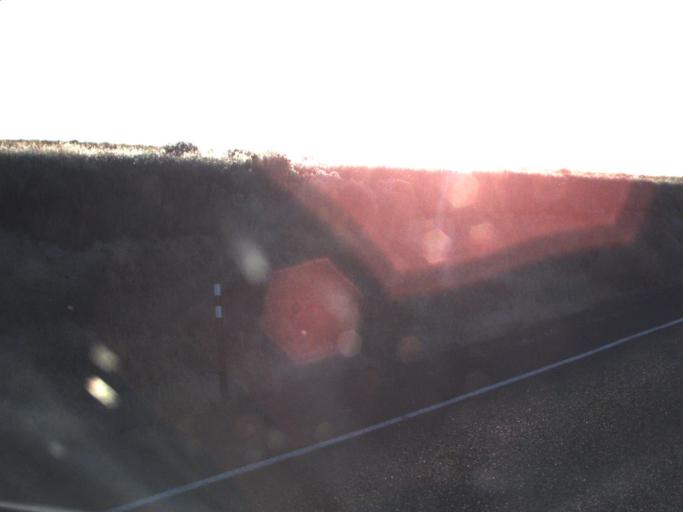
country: US
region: Washington
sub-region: Franklin County
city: Connell
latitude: 46.7103
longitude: -118.5321
